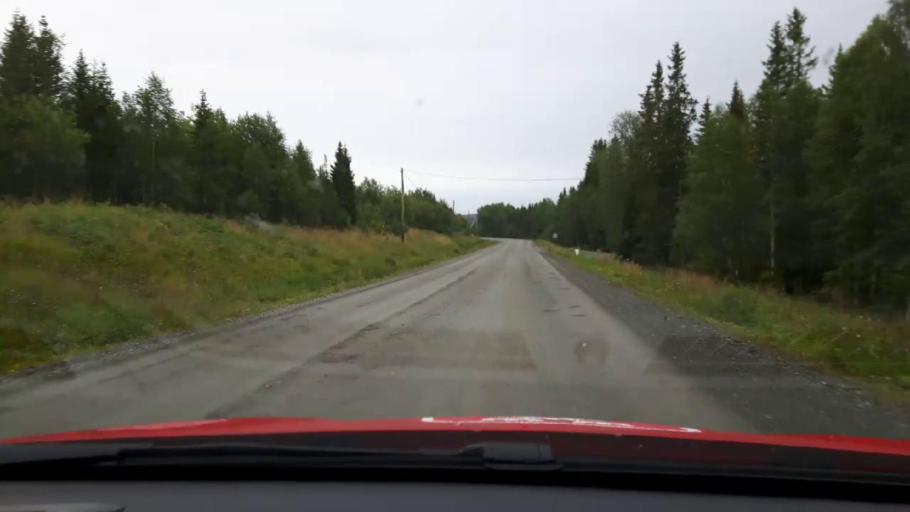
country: SE
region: Jaemtland
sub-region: Are Kommun
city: Are
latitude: 63.4561
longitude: 12.6436
